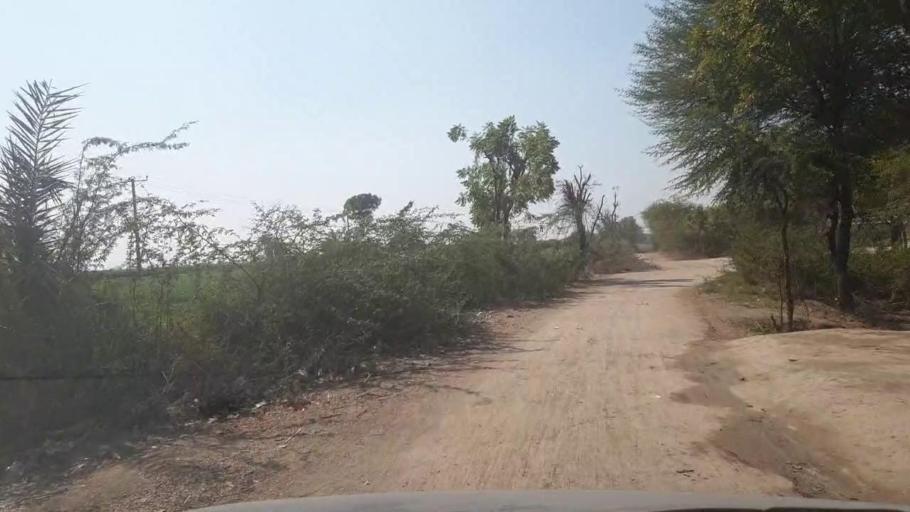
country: PK
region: Sindh
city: Chambar
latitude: 25.2305
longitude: 68.8499
